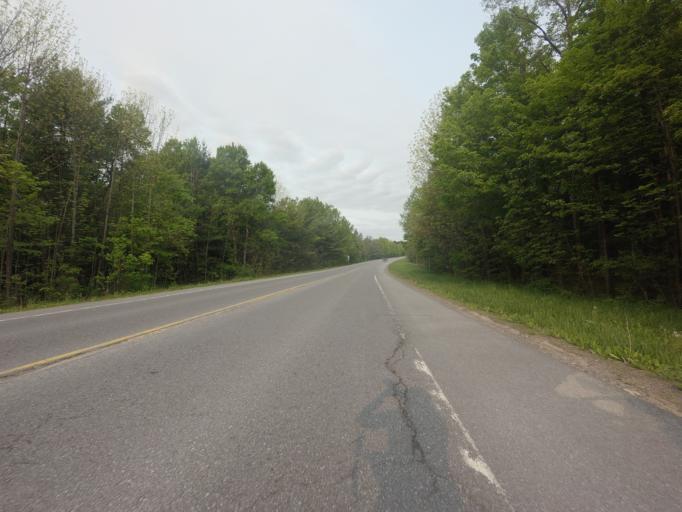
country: US
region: New York
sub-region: Jefferson County
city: Carthage
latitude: 44.0330
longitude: -75.5990
